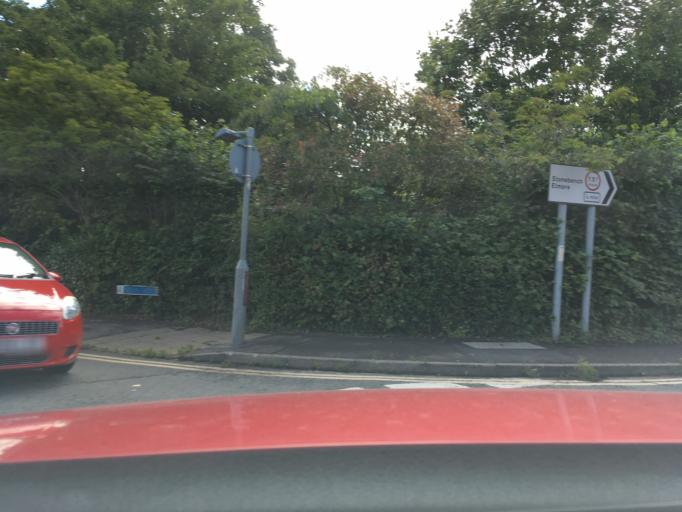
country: GB
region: England
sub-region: Gloucestershire
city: Gloucester
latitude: 51.8336
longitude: -2.2802
